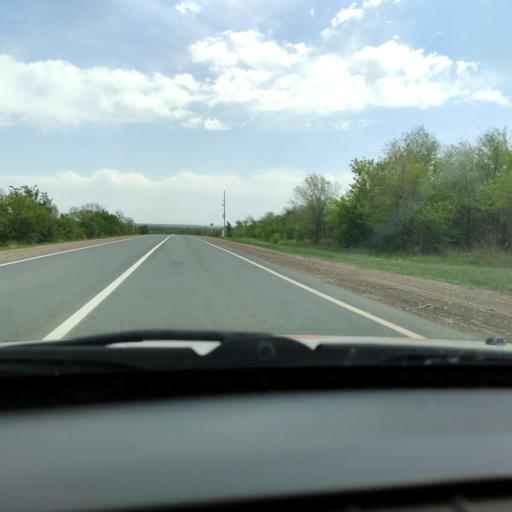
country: RU
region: Samara
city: Mirnyy
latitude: 53.6393
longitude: 50.2300
